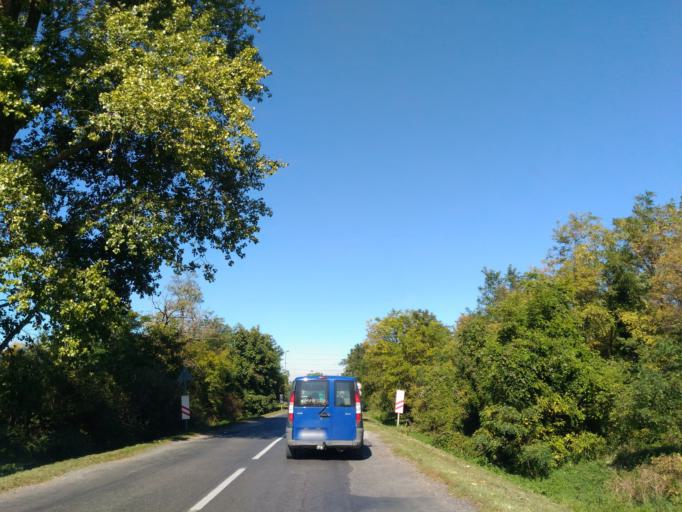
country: HU
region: Fejer
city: Ivancsa
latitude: 47.1752
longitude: 18.8115
